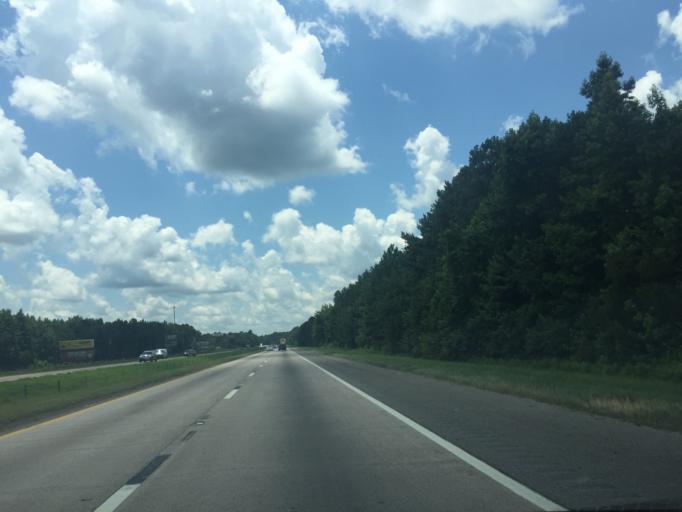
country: US
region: South Carolina
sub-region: Jasper County
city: Ridgeland
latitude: 32.4586
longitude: -80.9841
